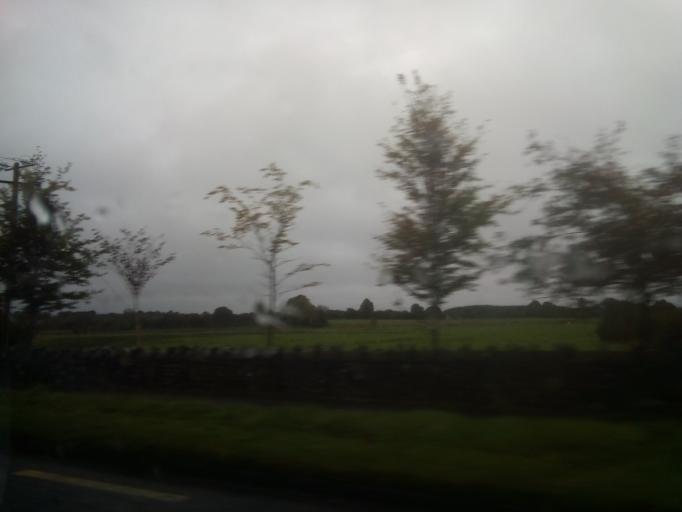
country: IE
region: Connaught
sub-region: Roscommon
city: Castlerea
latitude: 53.8669
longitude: -8.4034
